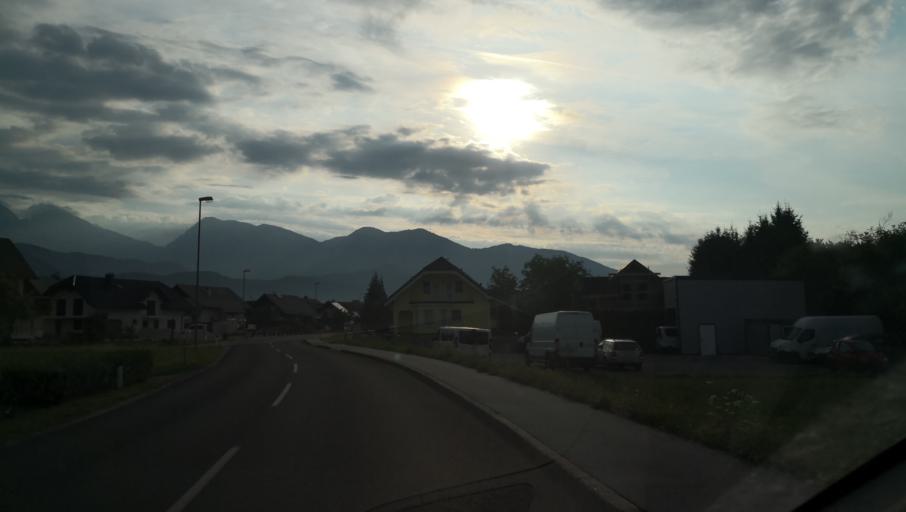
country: SI
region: Kranj
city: Britof
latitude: 46.2690
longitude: 14.4111
